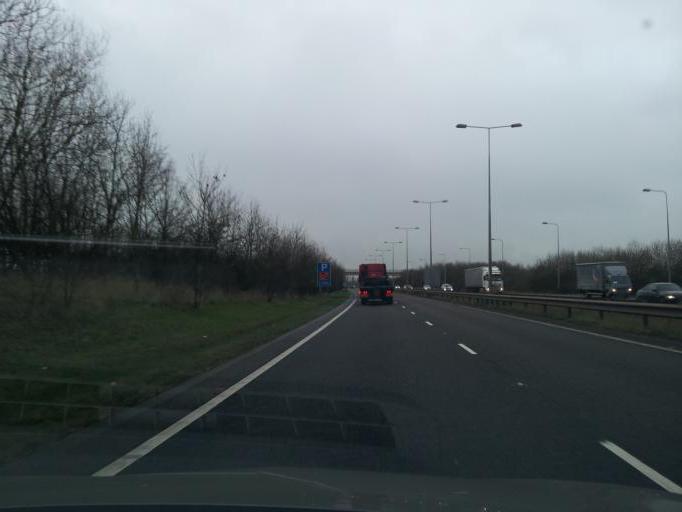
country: GB
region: England
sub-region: Derbyshire
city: Borrowash
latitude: 52.8689
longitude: -1.4016
